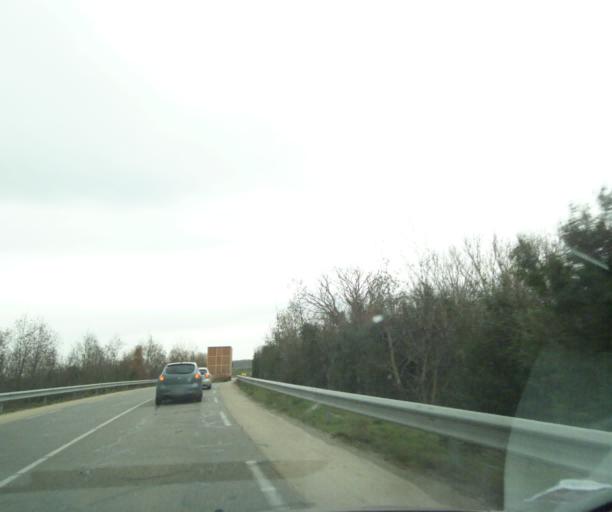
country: FR
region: Provence-Alpes-Cote d'Azur
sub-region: Departement des Bouches-du-Rhone
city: Meyrargues
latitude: 43.6482
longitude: 5.5460
